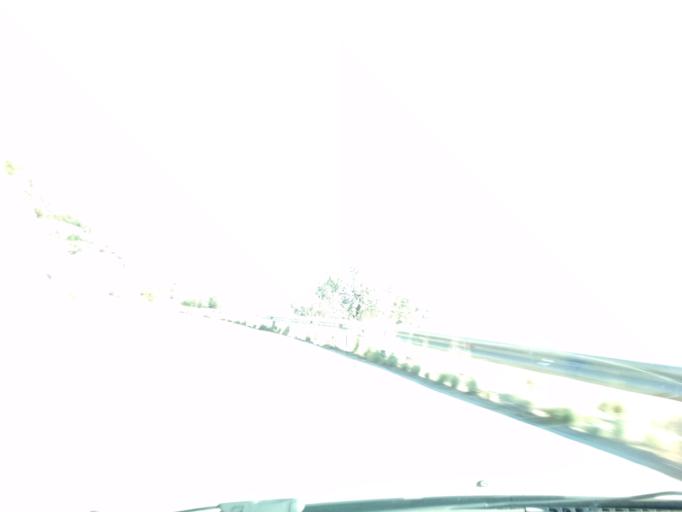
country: GR
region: Central Greece
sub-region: Nomos Evvoias
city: Oreoi
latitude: 38.8431
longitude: 23.0750
